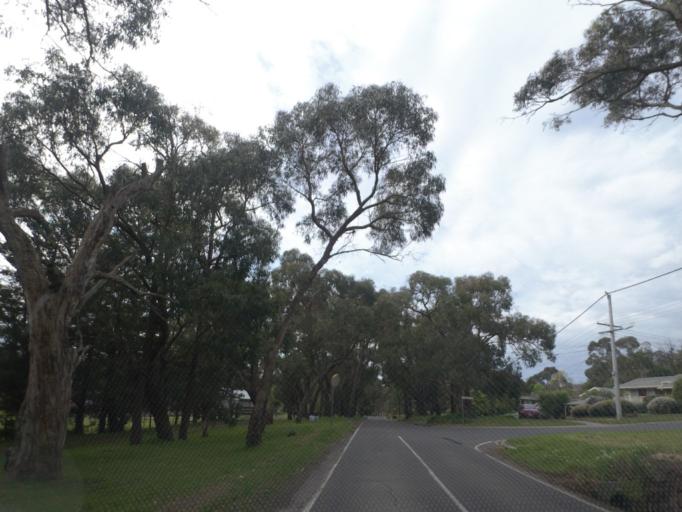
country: AU
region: Victoria
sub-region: Yarra Ranges
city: Montrose
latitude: -37.8291
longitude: 145.3350
